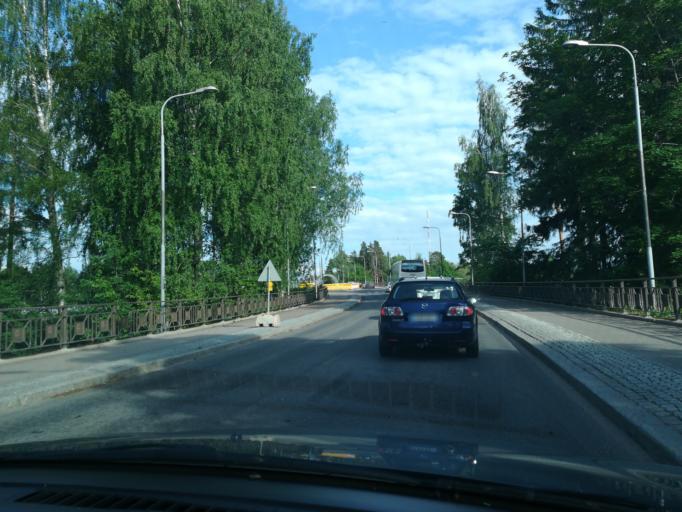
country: FI
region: South Karelia
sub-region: Imatra
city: Imatra
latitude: 61.1693
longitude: 28.7741
